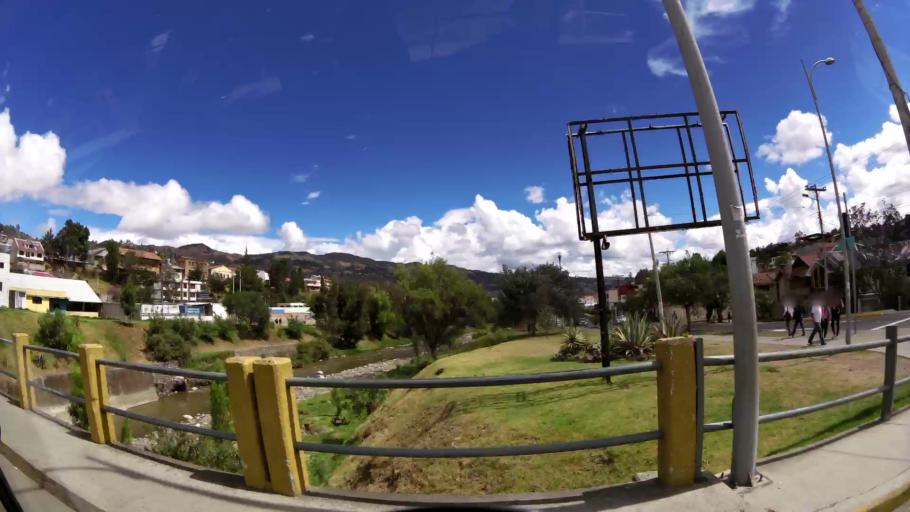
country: EC
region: Canar
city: Azogues
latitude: -2.7445
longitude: -78.8500
